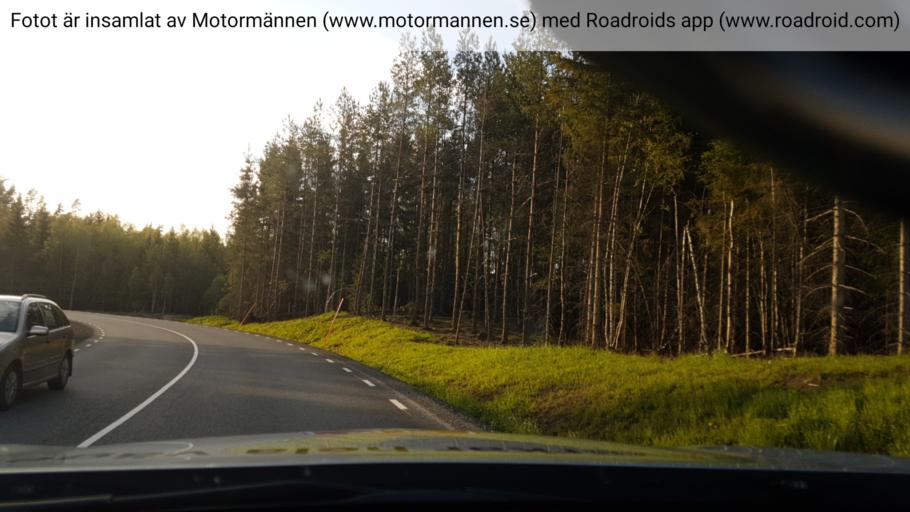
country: SE
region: Joenkoeping
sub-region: Mullsjo Kommun
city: Mullsjoe
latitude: 57.8874
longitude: 13.8995
